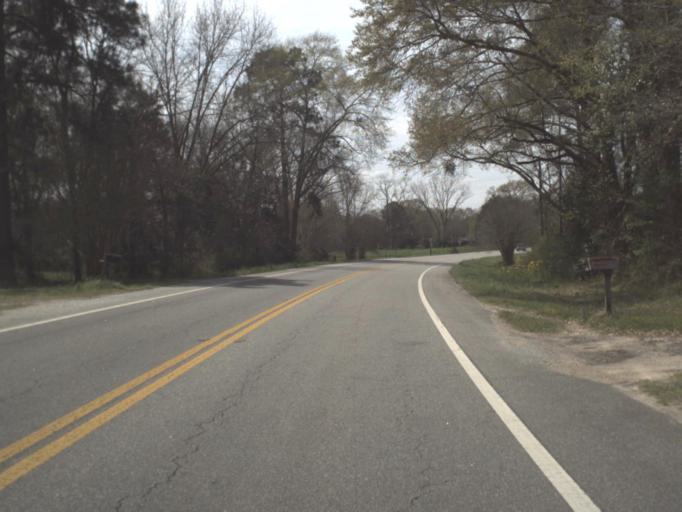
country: US
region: Florida
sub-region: Jackson County
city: Graceville
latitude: 30.9768
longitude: -85.4931
